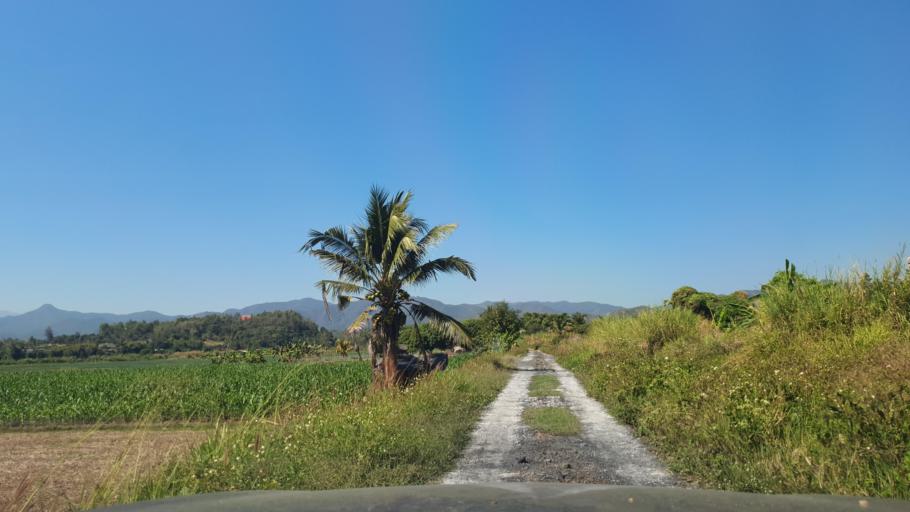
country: TH
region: Chiang Mai
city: Mae Wang
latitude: 18.6705
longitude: 98.8287
